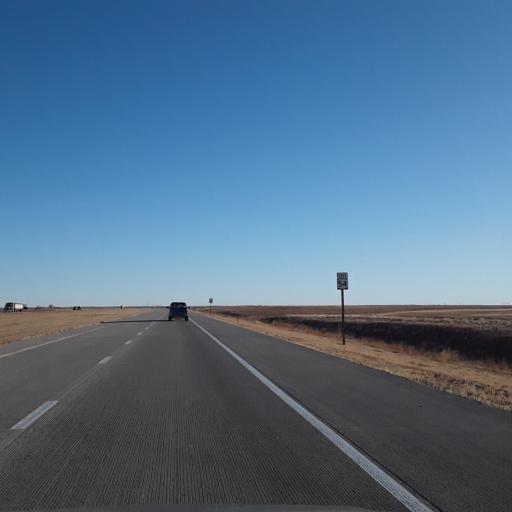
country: US
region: Kansas
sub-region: Seward County
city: Liberal
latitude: 37.1040
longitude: -100.7946
